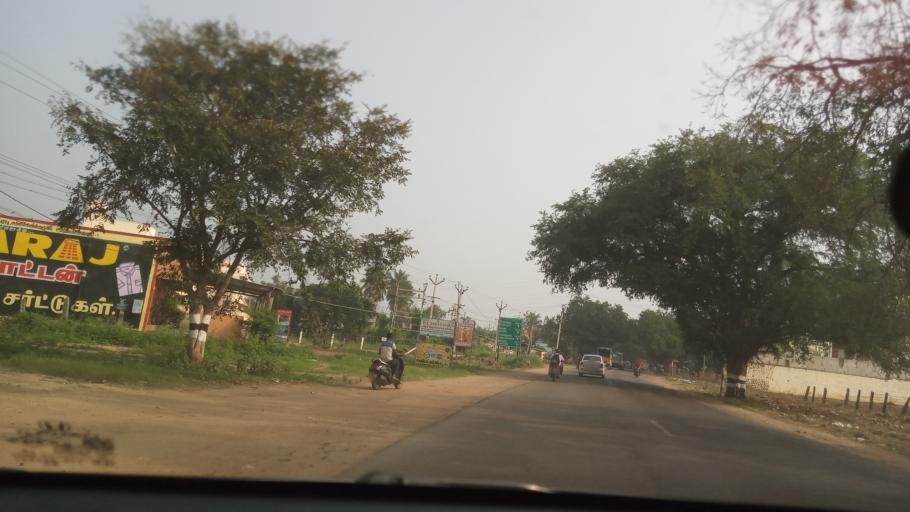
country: IN
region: Tamil Nadu
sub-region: Coimbatore
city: Annur
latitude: 11.1704
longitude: 77.0544
